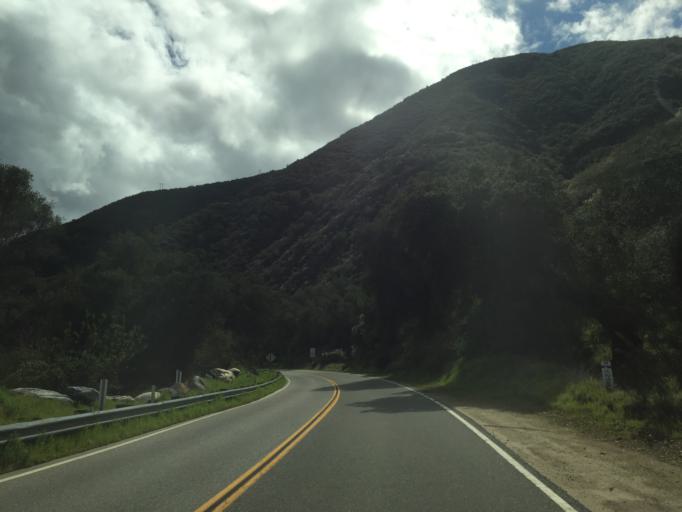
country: US
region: California
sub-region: Los Angeles County
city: Glendora
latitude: 34.2377
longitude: -117.8514
